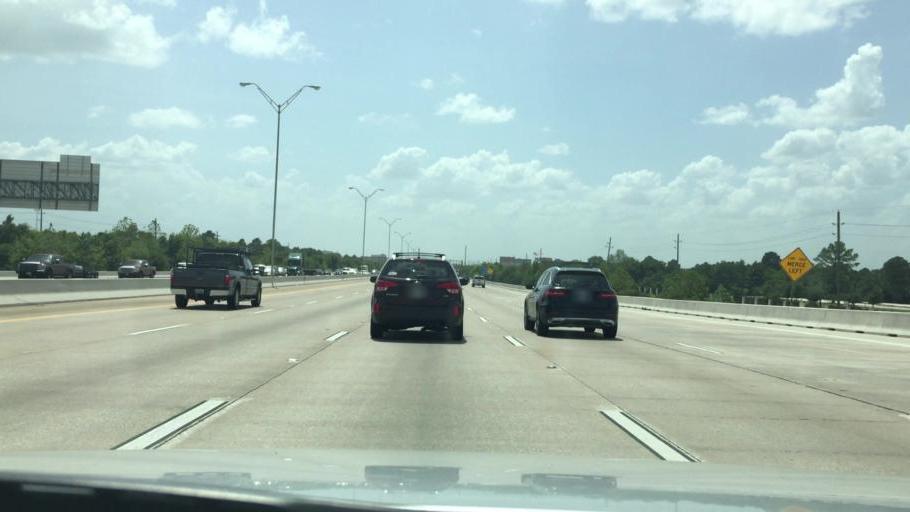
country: US
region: Texas
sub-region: Harris County
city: Hudson
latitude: 29.9351
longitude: -95.5316
